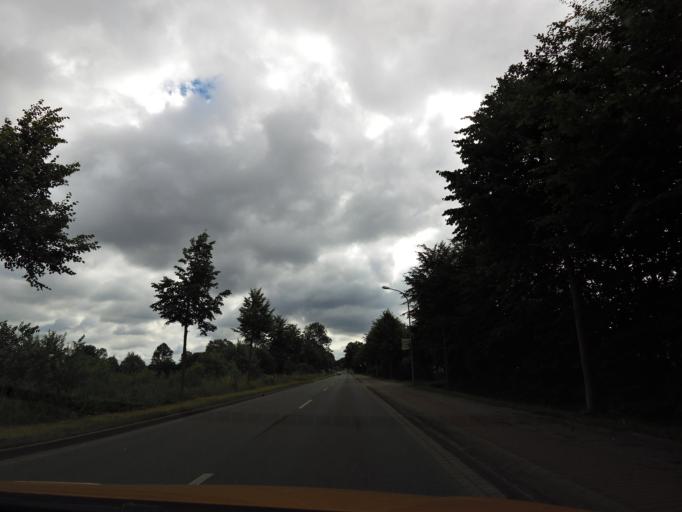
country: DE
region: Mecklenburg-Vorpommern
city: Guestrow
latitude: 53.7846
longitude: 12.1927
